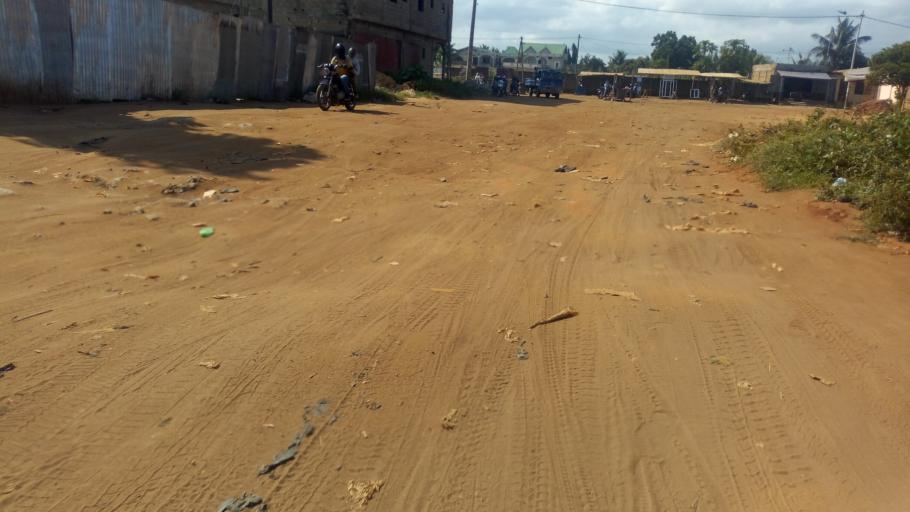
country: TG
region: Maritime
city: Lome
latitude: 6.2244
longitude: 1.1887
